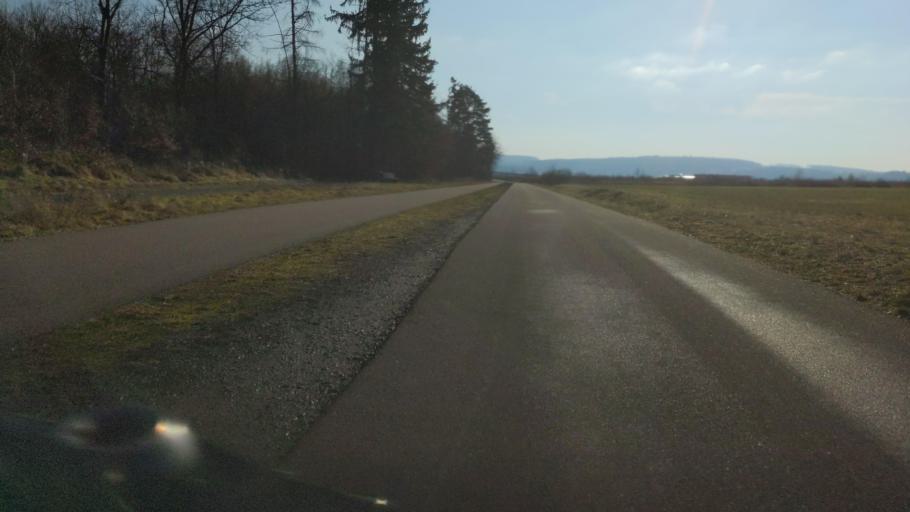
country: DE
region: Baden-Wuerttemberg
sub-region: Regierungsbezirk Stuttgart
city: Renningen
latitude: 48.7861
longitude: 8.9248
